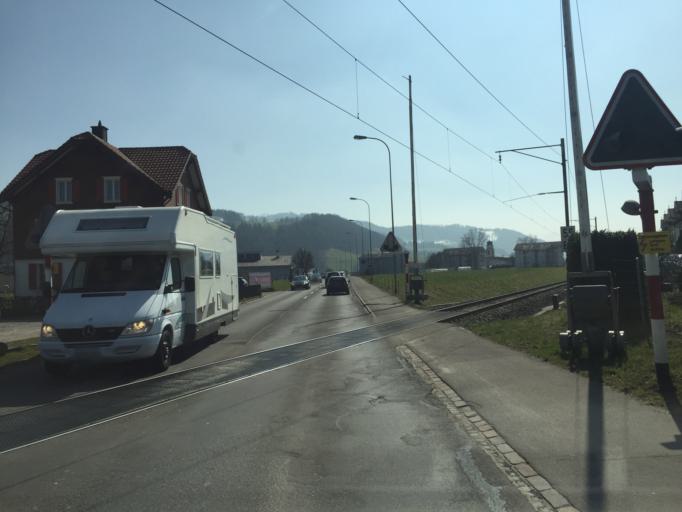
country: CH
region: Saint Gallen
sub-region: Wahlkreis Toggenburg
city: Buetschwil
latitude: 47.3507
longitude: 9.0769
